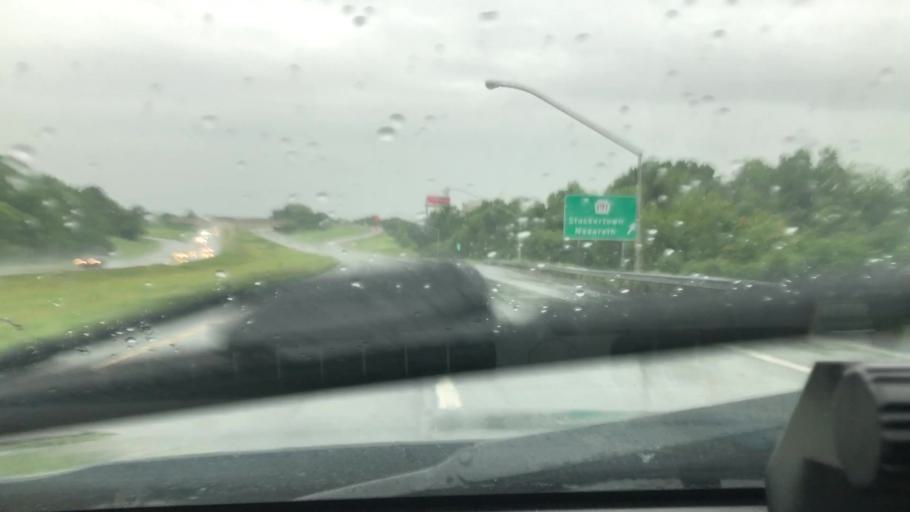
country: US
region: Pennsylvania
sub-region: Northampton County
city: Belfast
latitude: 40.7598
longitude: -75.2729
